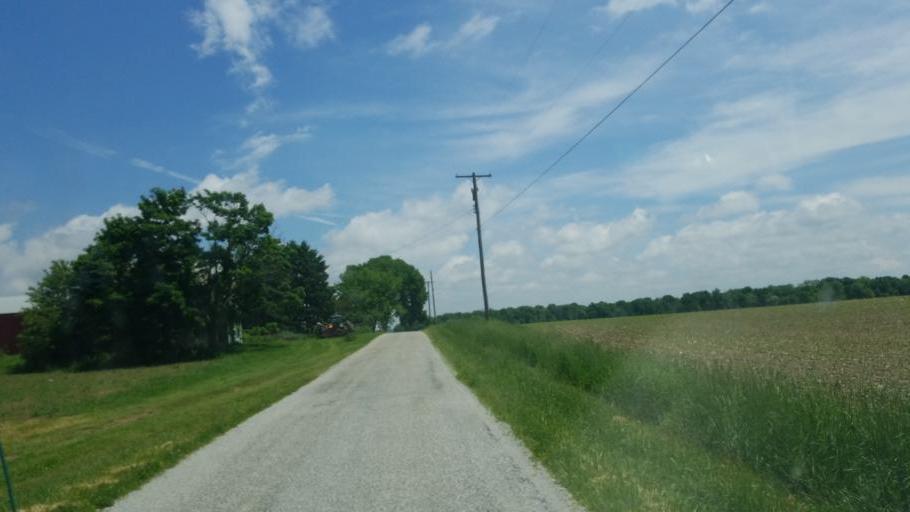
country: US
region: Ohio
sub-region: Wayne County
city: West Salem
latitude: 40.8425
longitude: -82.1688
